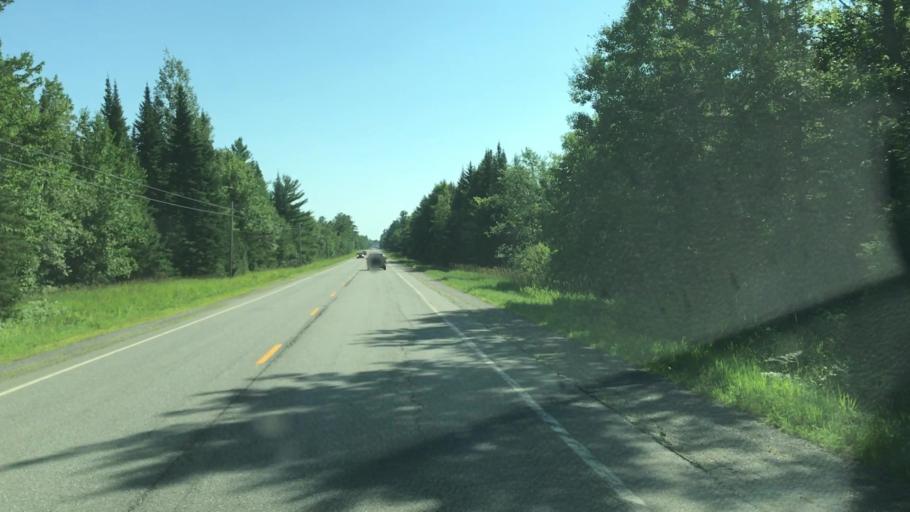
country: US
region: Maine
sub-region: Penobscot County
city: Enfield
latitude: 45.3107
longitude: -68.6079
